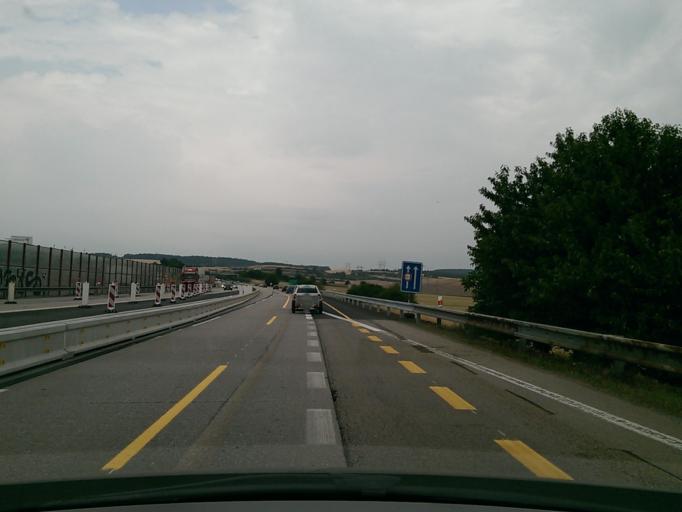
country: CZ
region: South Moravian
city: Ricany
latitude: 49.2165
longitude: 16.4103
